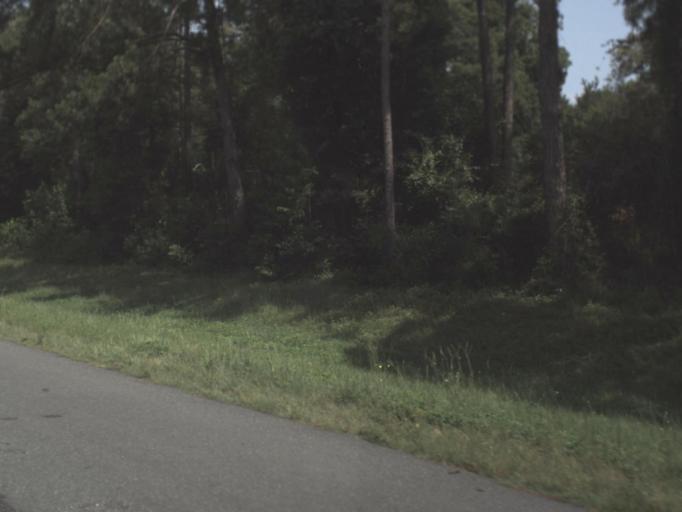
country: US
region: Florida
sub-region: Hamilton County
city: Jasper
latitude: 30.4923
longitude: -83.0262
